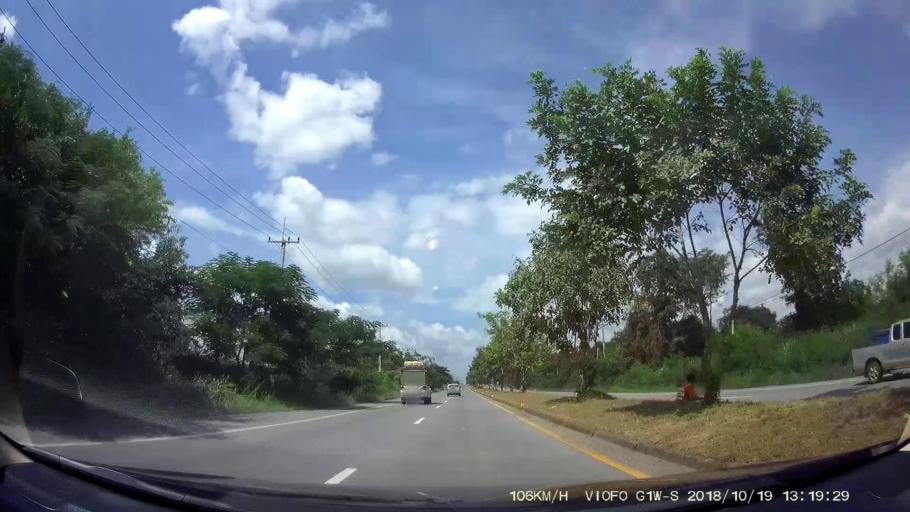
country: TH
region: Chaiyaphum
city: Chatturat
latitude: 15.4304
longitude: 101.8309
